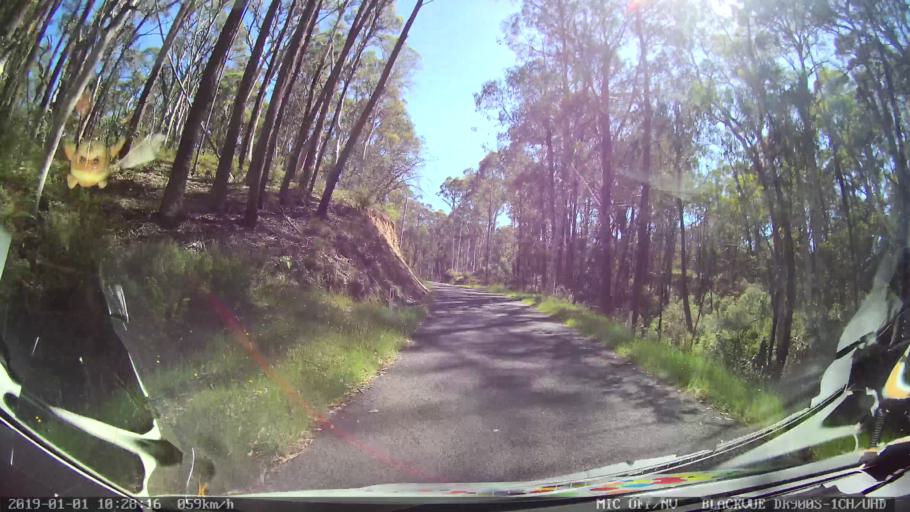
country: AU
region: New South Wales
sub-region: Snowy River
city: Jindabyne
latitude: -36.0613
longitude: 148.2394
